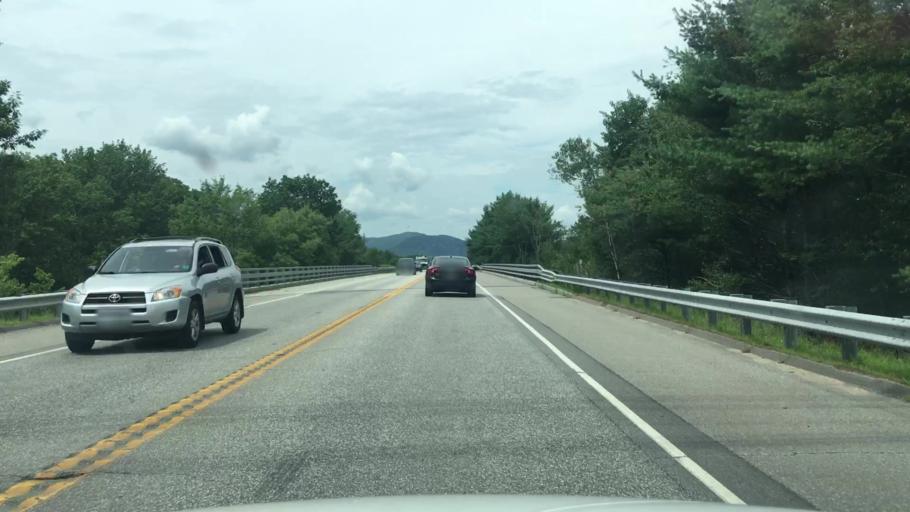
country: US
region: New Hampshire
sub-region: Grafton County
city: Plymouth
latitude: 43.7693
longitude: -71.7103
